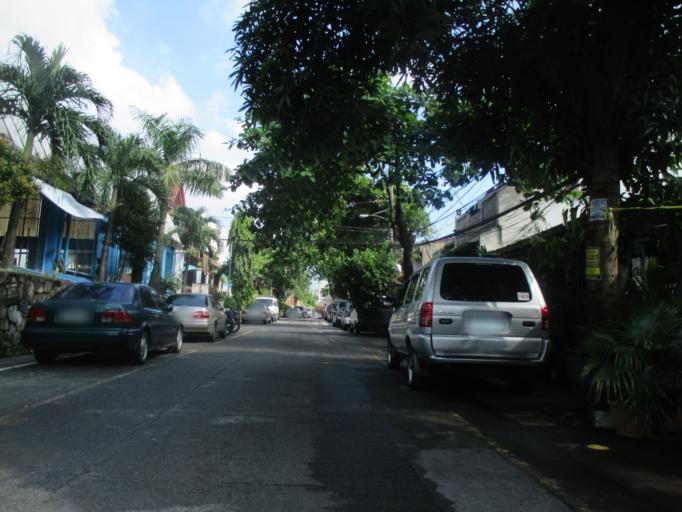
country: PH
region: Metro Manila
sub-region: Marikina
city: Calumpang
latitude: 14.6340
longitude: 121.0820
